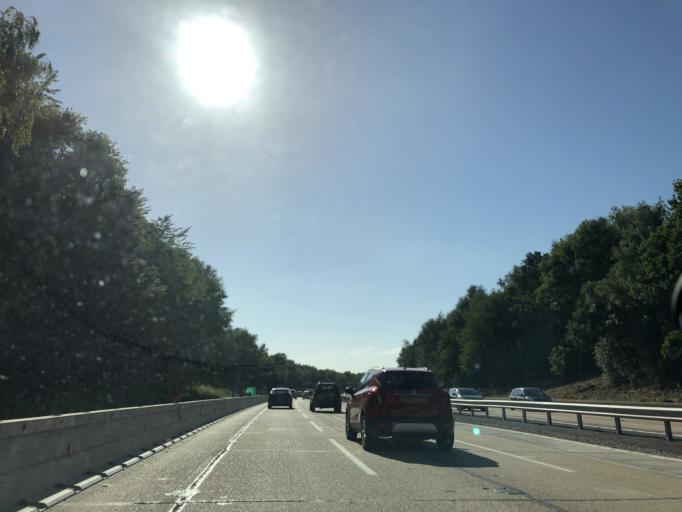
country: GB
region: England
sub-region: Hampshire
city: West End
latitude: 50.9355
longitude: -1.3421
